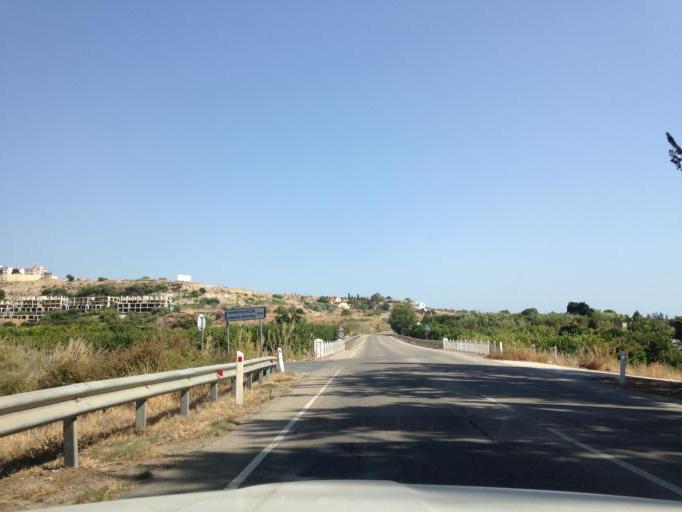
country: CY
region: Limassol
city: Pissouri
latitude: 34.7097
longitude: 32.5630
